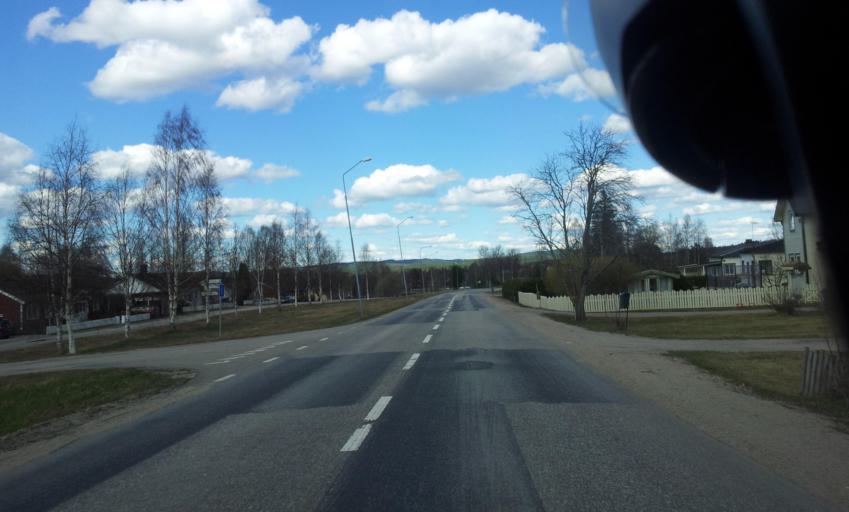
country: SE
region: Gaevleborg
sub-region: Ovanakers Kommun
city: Edsbyn
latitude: 61.3636
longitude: 15.8158
